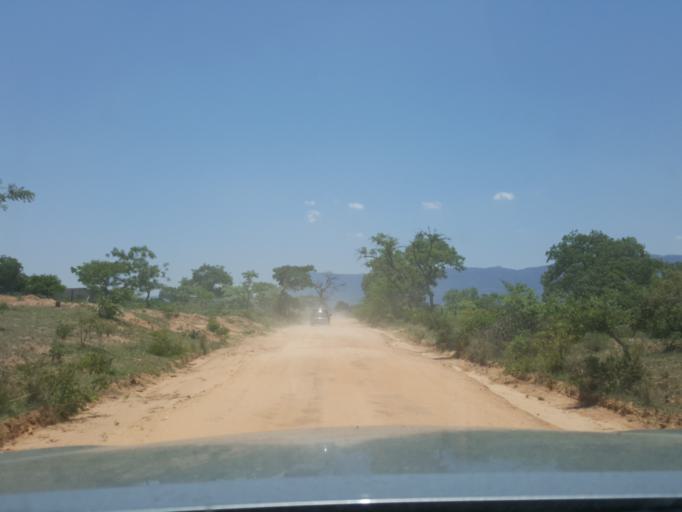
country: ZA
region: Limpopo
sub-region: Mopani District Municipality
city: Hoedspruit
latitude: -24.5799
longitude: 30.9912
